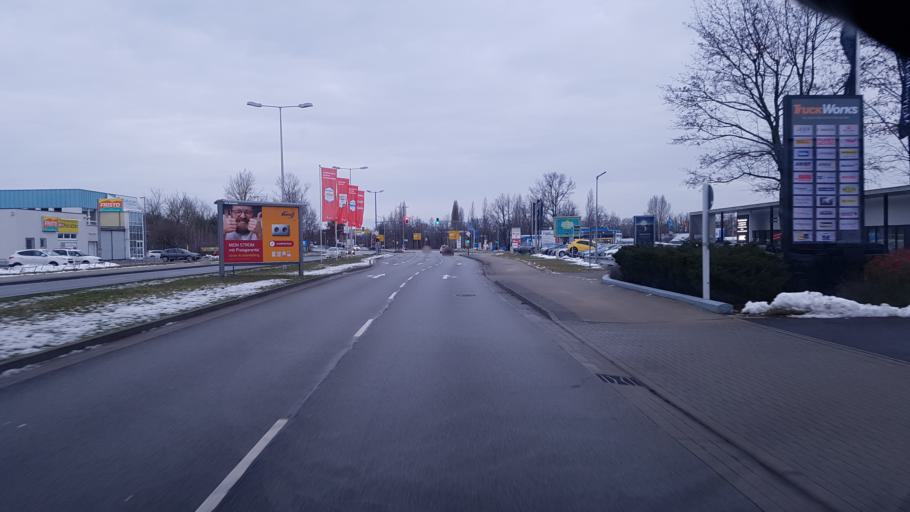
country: DE
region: Brandenburg
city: Cottbus
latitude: 51.7654
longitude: 14.3586
